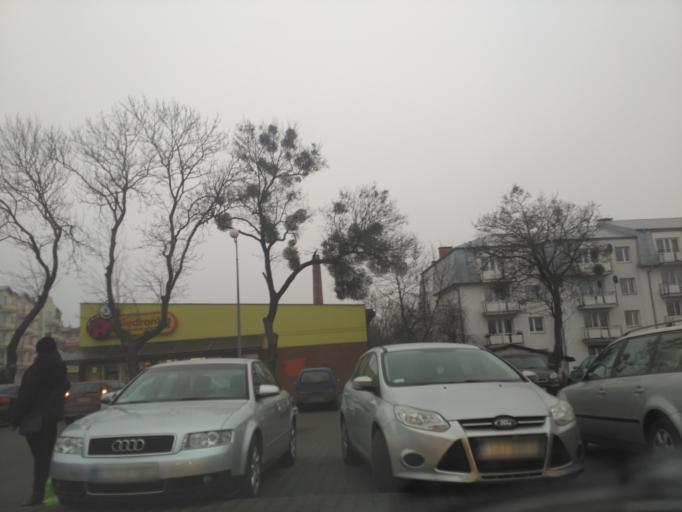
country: PL
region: Lublin Voivodeship
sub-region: Chelm
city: Chelm
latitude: 51.1305
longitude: 23.4737
